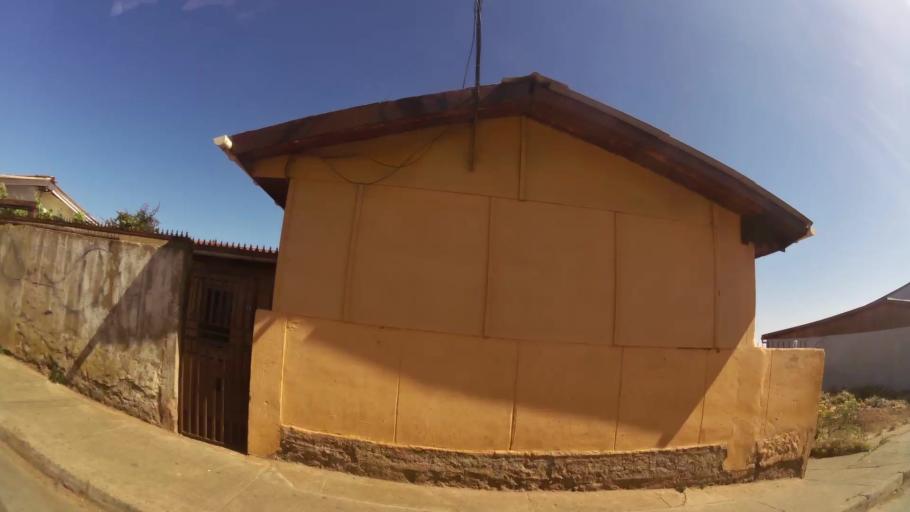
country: CL
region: Valparaiso
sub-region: Provincia de Valparaiso
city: Valparaiso
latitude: -33.0452
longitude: -71.6531
